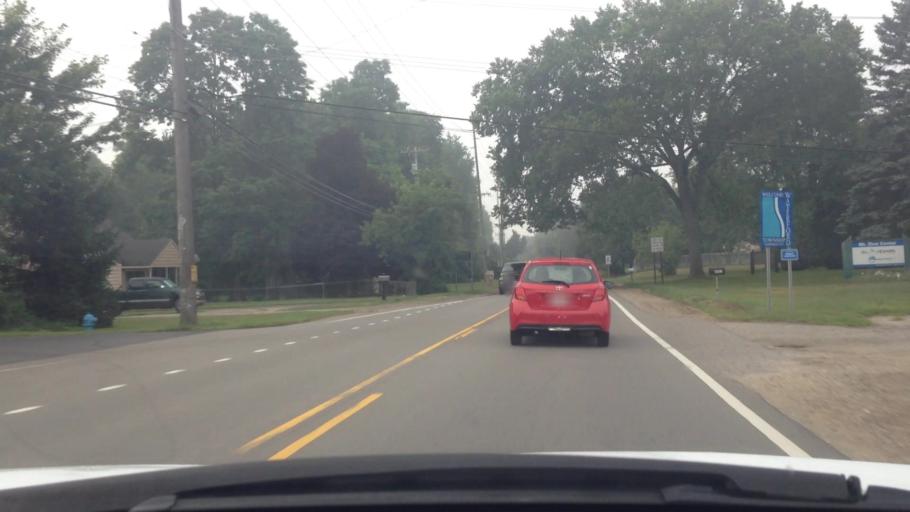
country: US
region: Michigan
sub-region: Oakland County
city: Waterford
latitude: 42.7051
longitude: -83.3487
